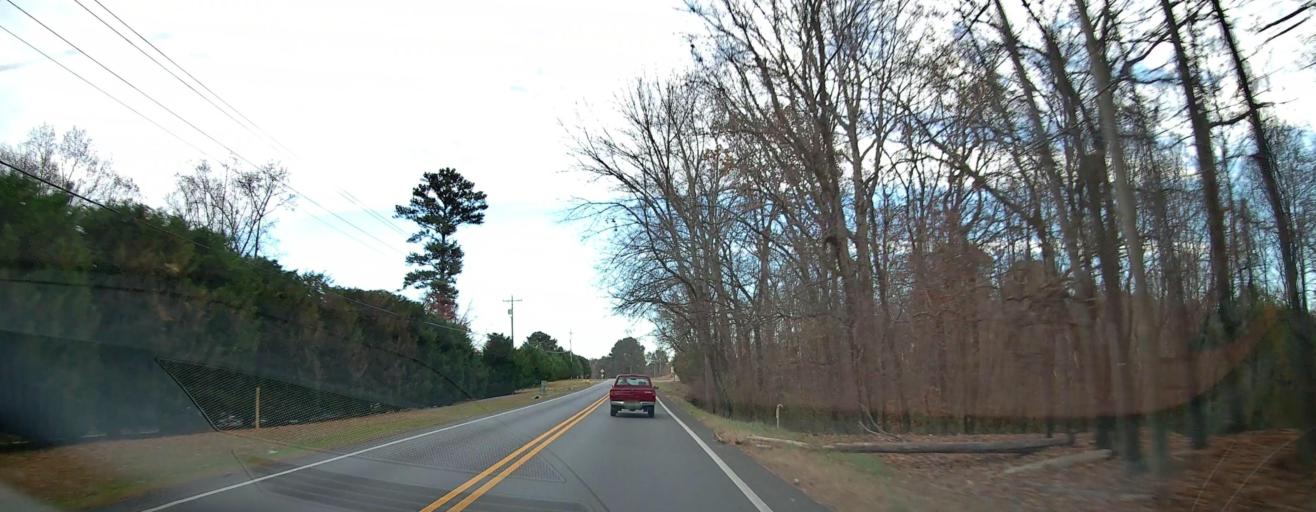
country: US
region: Alabama
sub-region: Morgan County
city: Priceville
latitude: 34.4899
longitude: -86.8382
